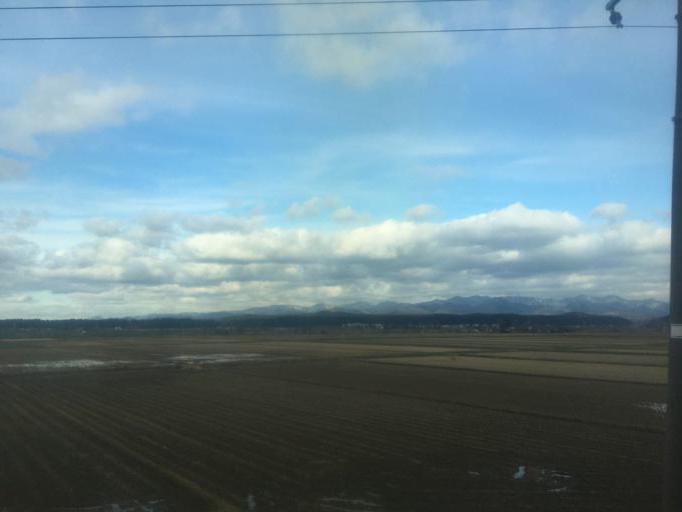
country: JP
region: Akita
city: Noshiromachi
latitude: 40.2122
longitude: 140.1400
